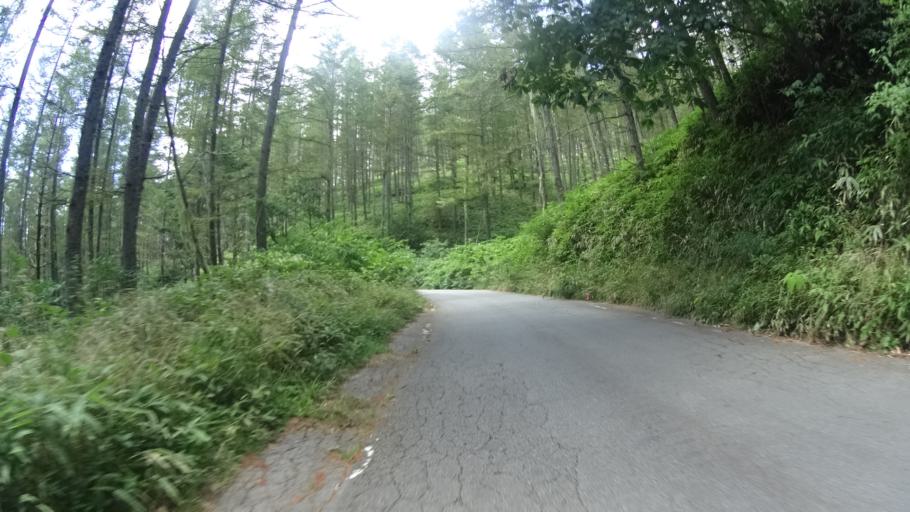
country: JP
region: Yamanashi
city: Enzan
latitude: 35.8232
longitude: 138.6488
